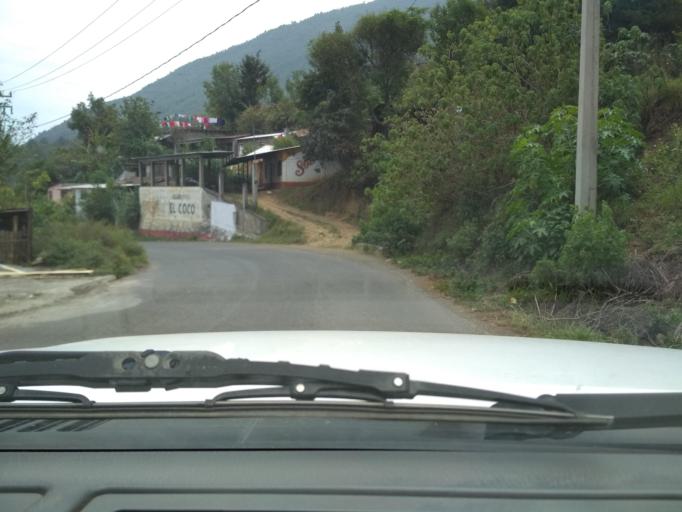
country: MX
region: Veracruz
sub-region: Camerino Z. Mendoza
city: La Cuesta
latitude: 18.7902
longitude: -97.1662
